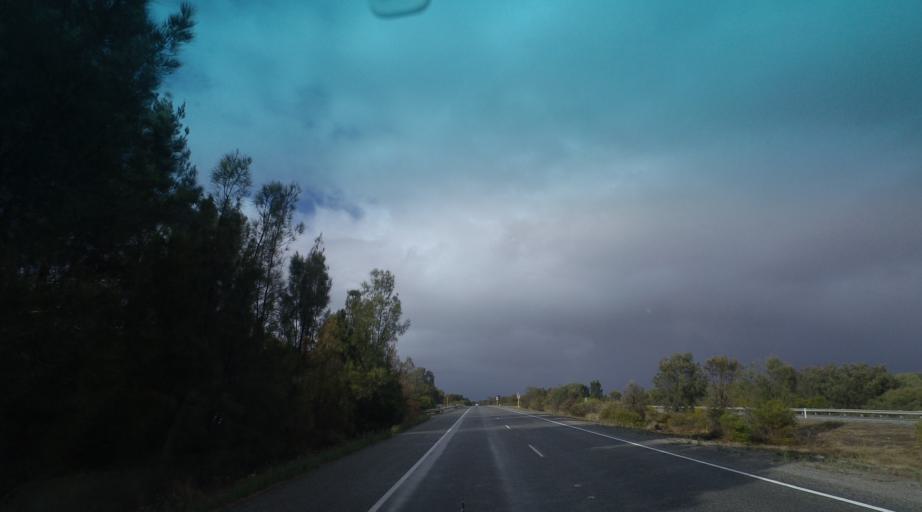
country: AU
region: Western Australia
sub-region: Serpentine-Jarrahdale
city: Oakford
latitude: -32.1915
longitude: 115.9625
